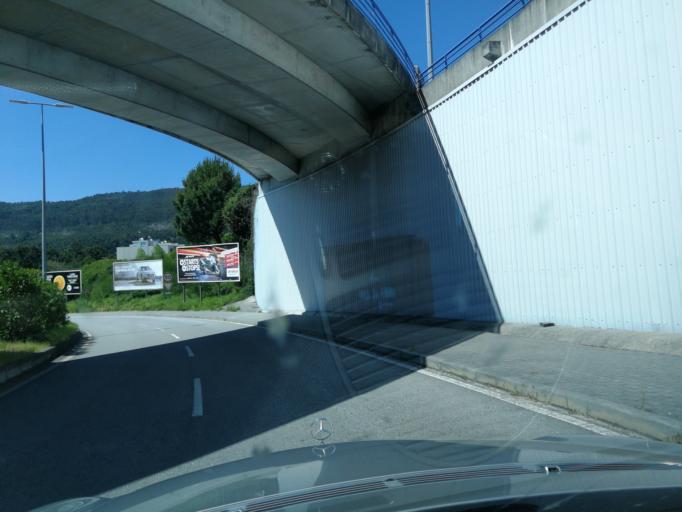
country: PT
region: Viana do Castelo
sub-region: Viana do Castelo
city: Meadela
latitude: 41.7112
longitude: -8.8092
